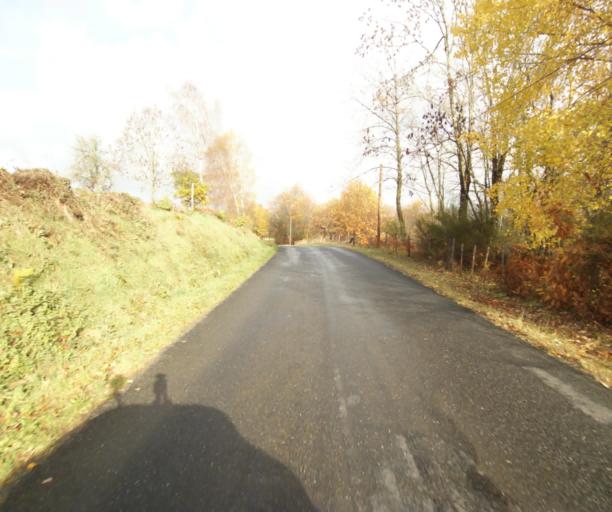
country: FR
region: Limousin
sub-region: Departement de la Correze
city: Cornil
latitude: 45.2039
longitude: 1.6398
